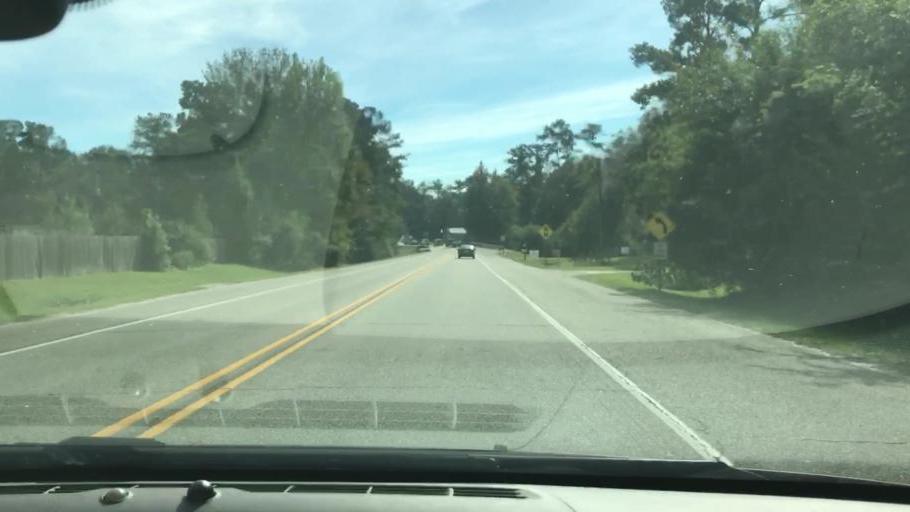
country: US
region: Louisiana
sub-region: Saint Tammany Parish
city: Pearl River
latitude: 30.3747
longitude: -89.7675
